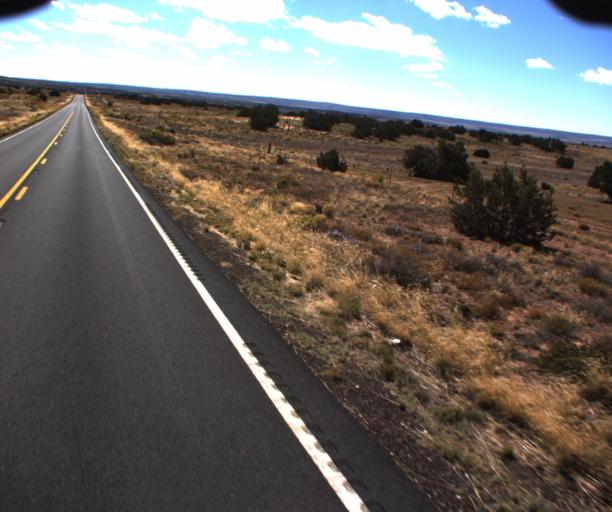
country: US
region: Arizona
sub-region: Apache County
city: Houck
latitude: 35.1168
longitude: -109.3221
